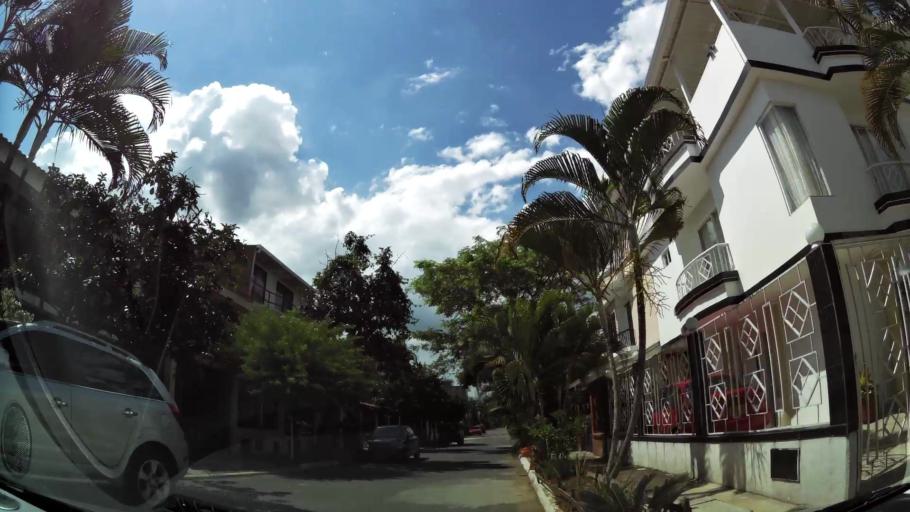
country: CO
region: Valle del Cauca
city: Cali
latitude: 3.3948
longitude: -76.5160
